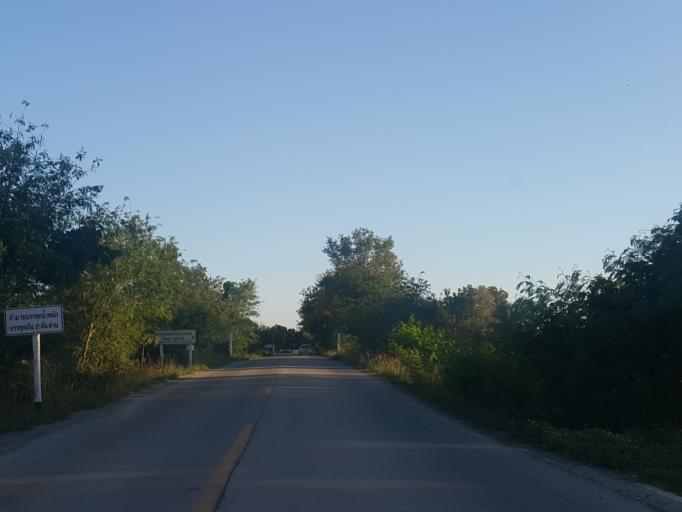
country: TH
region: Chiang Mai
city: San Sai
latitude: 18.8841
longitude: 99.1557
